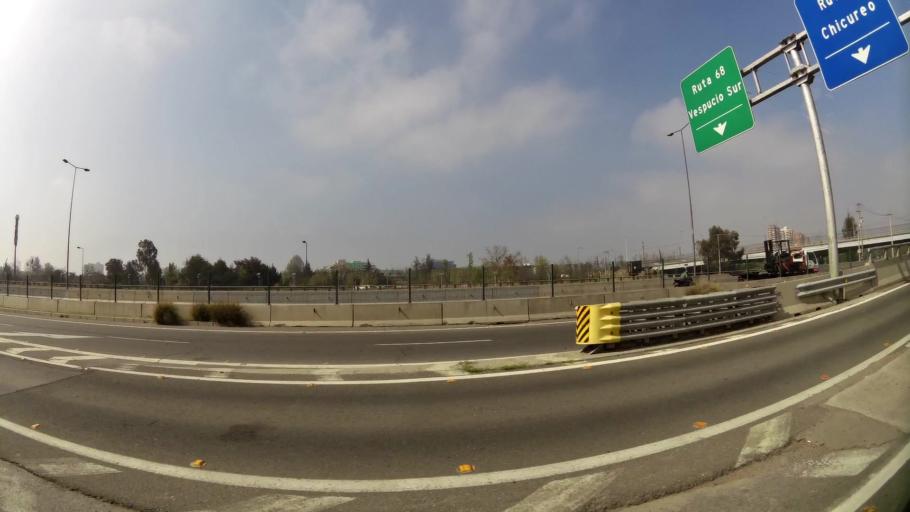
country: CL
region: Santiago Metropolitan
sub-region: Provincia de Santiago
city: Villa Presidente Frei, Nunoa, Santiago, Chile
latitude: -33.3887
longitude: -70.5982
